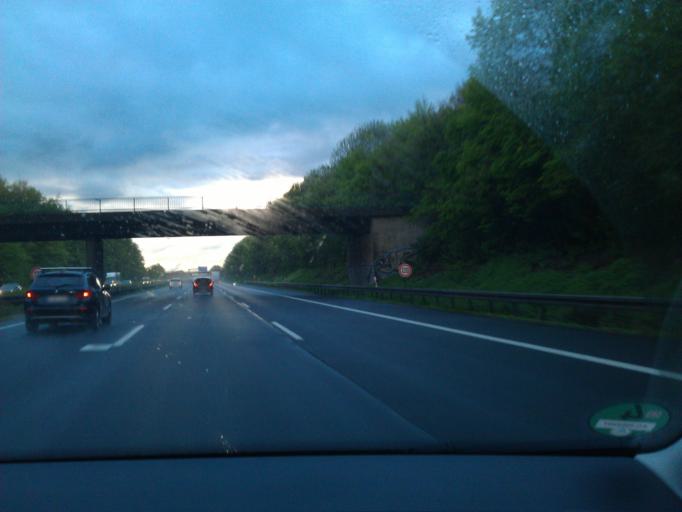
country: DE
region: North Rhine-Westphalia
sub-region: Regierungsbezirk Koln
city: Hurth
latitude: 50.9090
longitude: 6.8864
